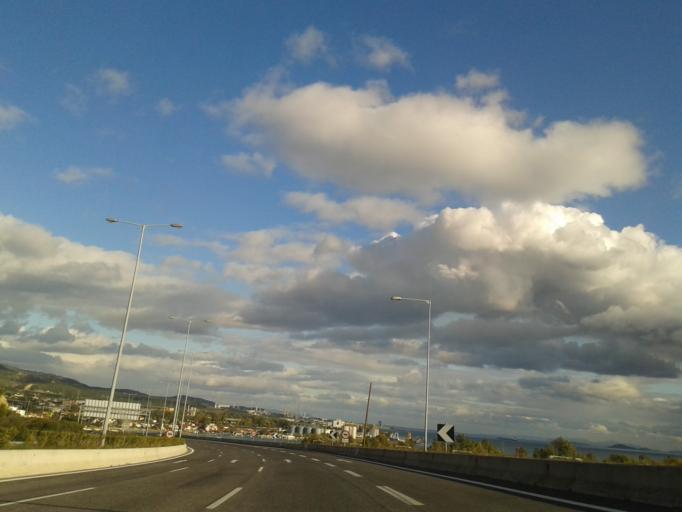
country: GR
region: Peloponnese
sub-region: Nomos Korinthias
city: Isthmia
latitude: 37.9224
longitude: 23.0061
